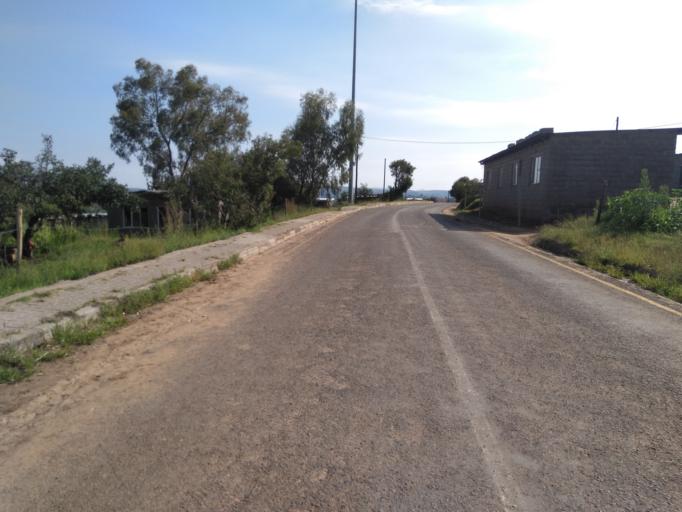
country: LS
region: Butha-Buthe
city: Butha-Buthe
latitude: -28.7759
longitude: 28.2459
